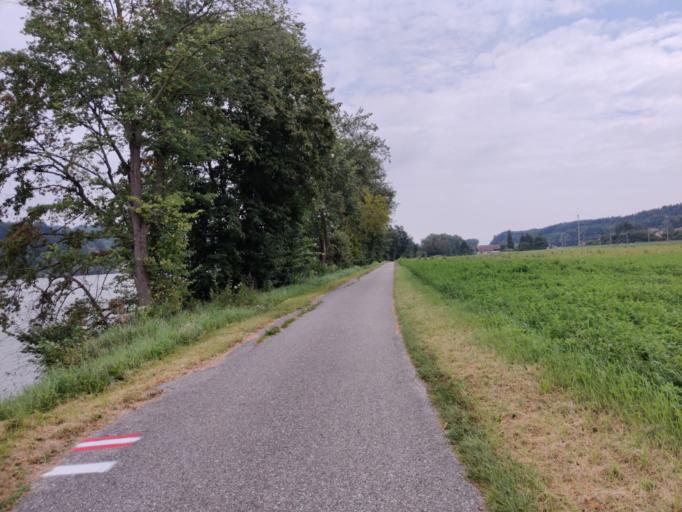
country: AT
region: Lower Austria
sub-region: Politischer Bezirk Melk
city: Marbach an der Donau
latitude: 48.2081
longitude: 15.1278
